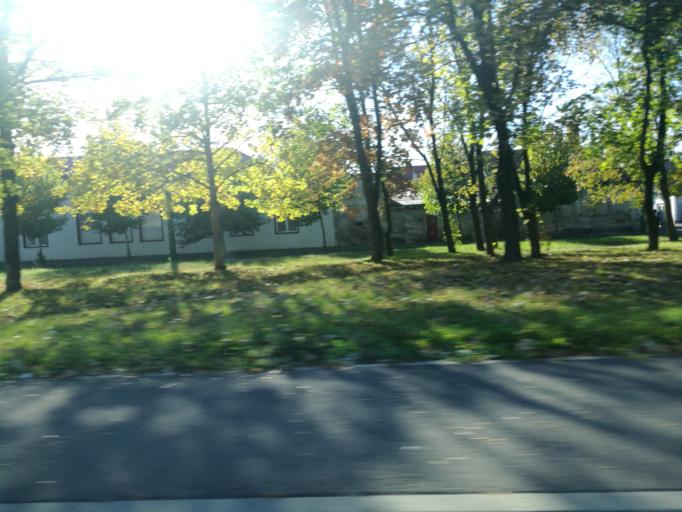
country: RO
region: Brasov
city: Brasov
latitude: 45.6641
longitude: 25.5927
